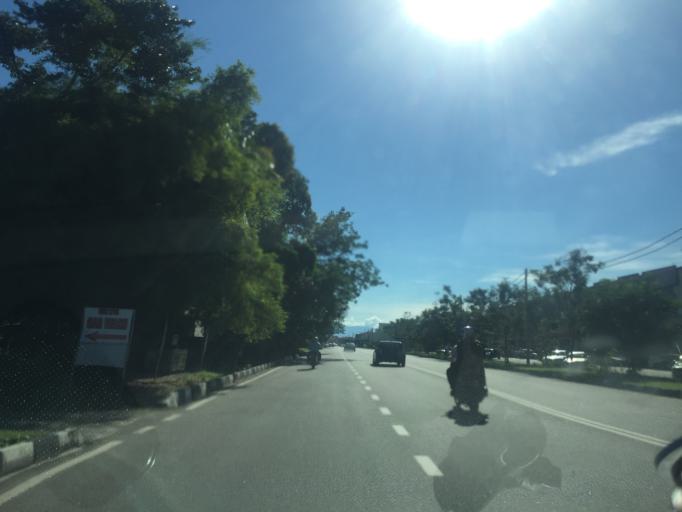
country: MY
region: Penang
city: Tasek Glugor
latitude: 5.5150
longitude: 100.5484
